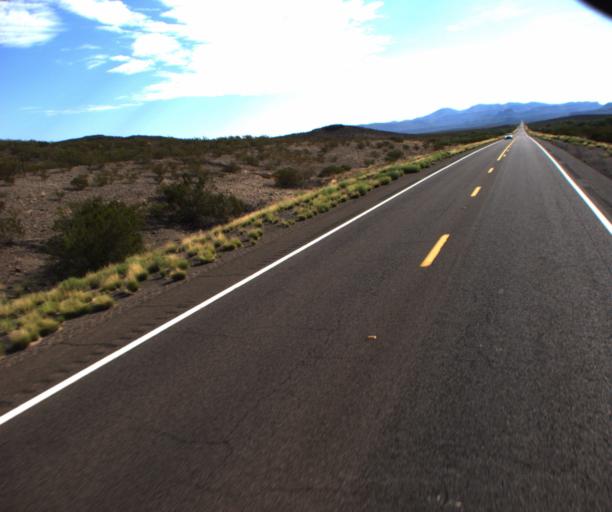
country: US
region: Arizona
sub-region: Graham County
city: Safford
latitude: 32.8029
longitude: -109.5218
